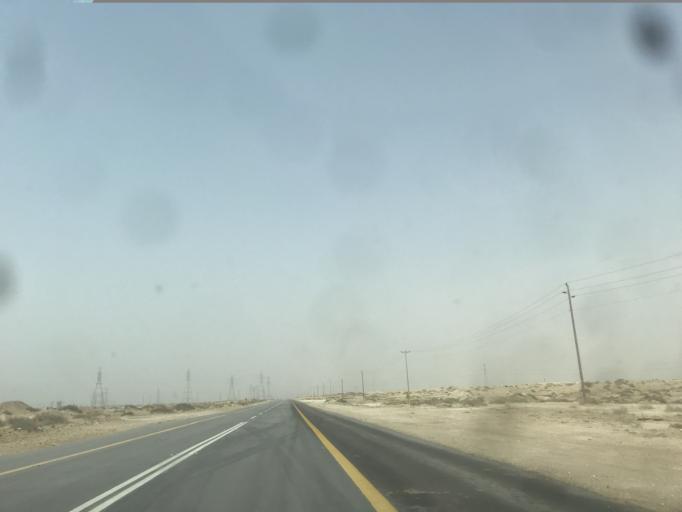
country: SA
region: Eastern Province
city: Abqaiq
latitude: 25.9352
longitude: 49.7286
